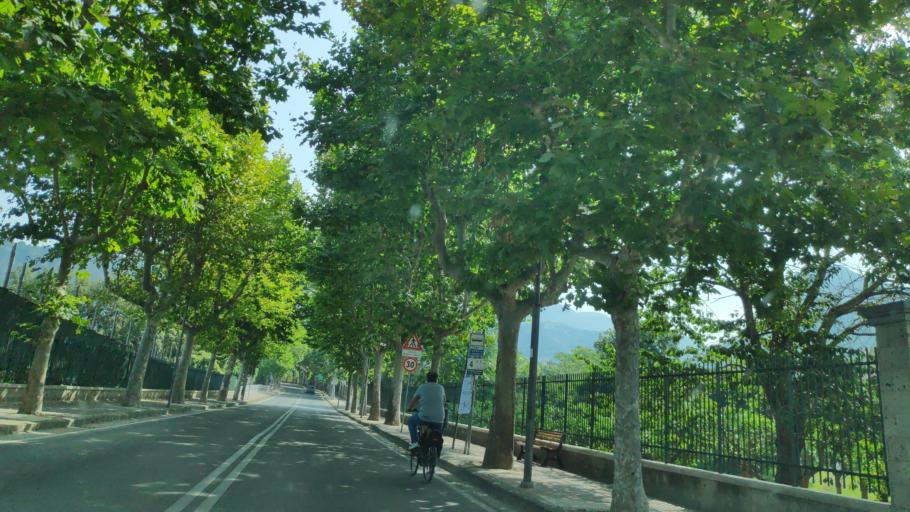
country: IT
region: Campania
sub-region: Provincia di Napoli
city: Piano di Sorrento
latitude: 40.6291
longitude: 14.4118
